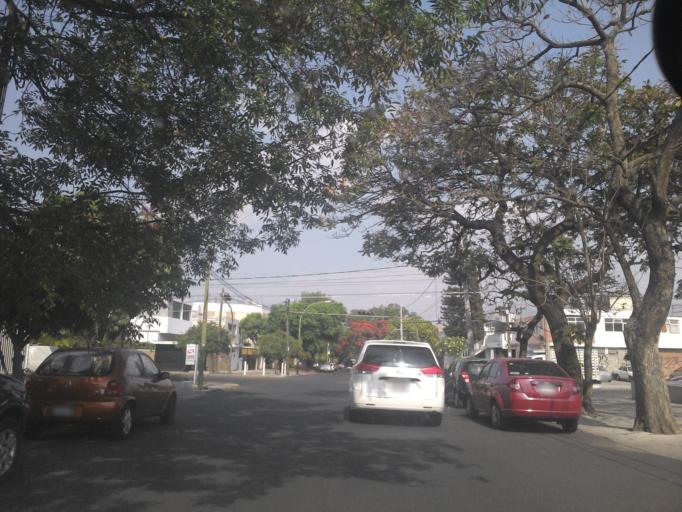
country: MX
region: Jalisco
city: Guadalajara
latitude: 20.6658
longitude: -103.3669
